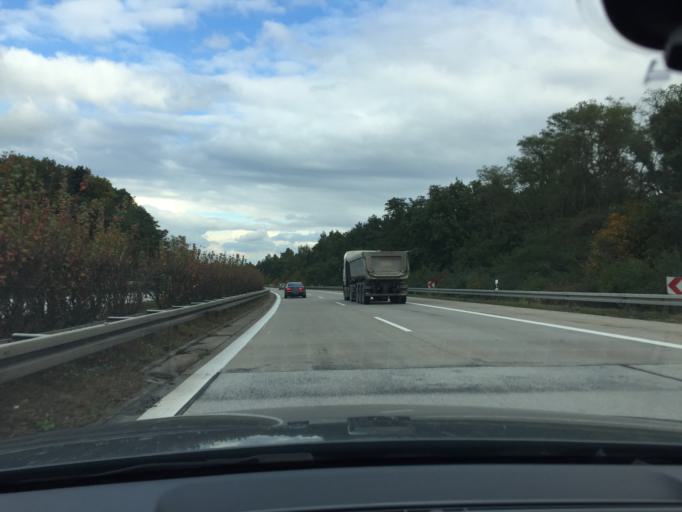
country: DE
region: Brandenburg
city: Ortrand
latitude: 51.3654
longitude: 13.7420
